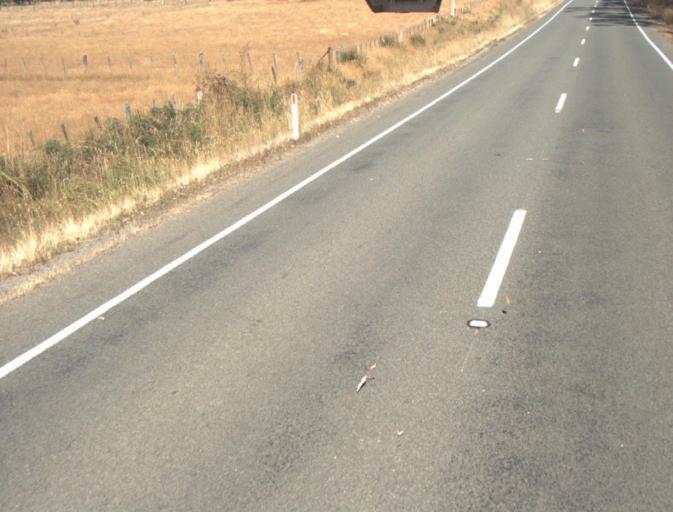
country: AU
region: Tasmania
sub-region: Launceston
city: Newstead
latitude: -41.3879
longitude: 147.3040
